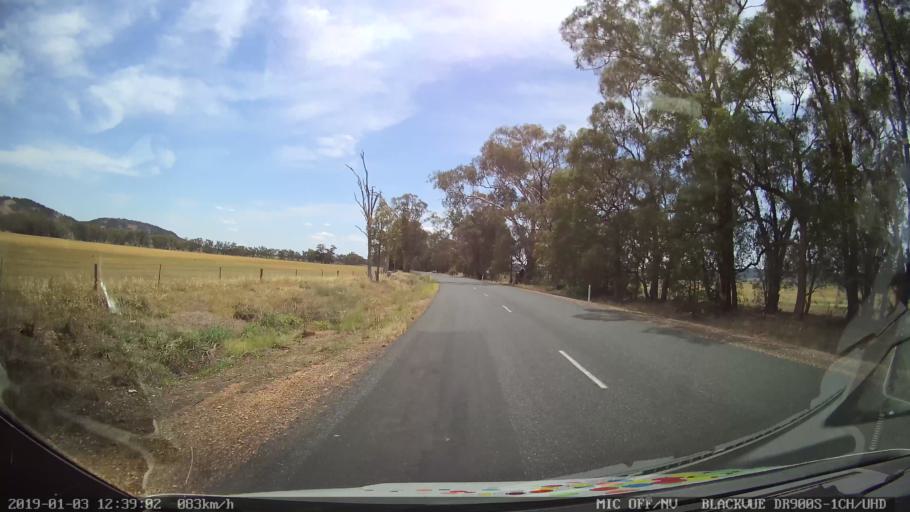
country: AU
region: New South Wales
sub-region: Weddin
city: Grenfell
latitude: -33.8286
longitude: 148.2025
